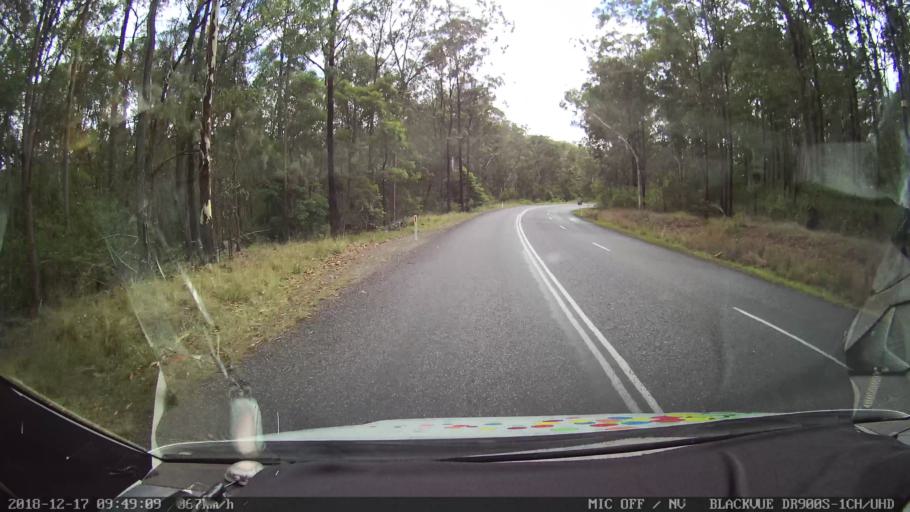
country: AU
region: New South Wales
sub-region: Tenterfield Municipality
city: Carrolls Creek
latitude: -28.9239
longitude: 152.3491
